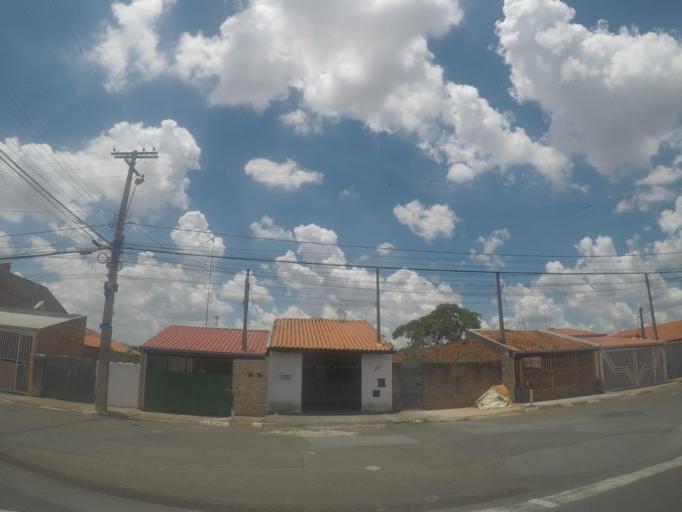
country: BR
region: Sao Paulo
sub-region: Sumare
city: Sumare
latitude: -22.8159
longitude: -47.2361
